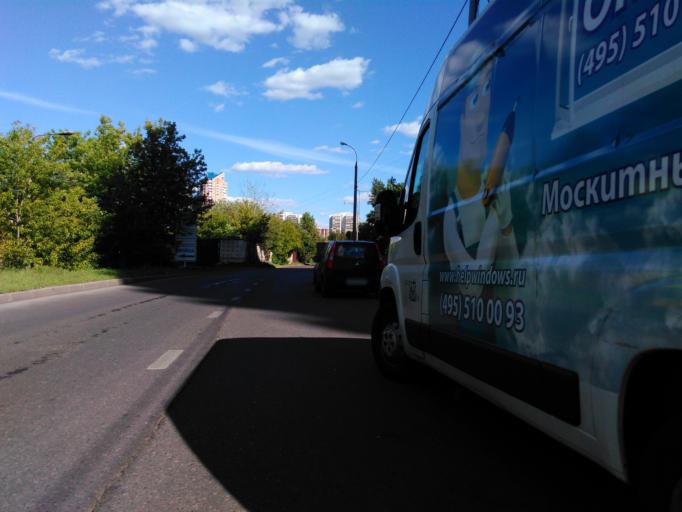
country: RU
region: Moscow
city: Troparevo
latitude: 55.6673
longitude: 37.4976
